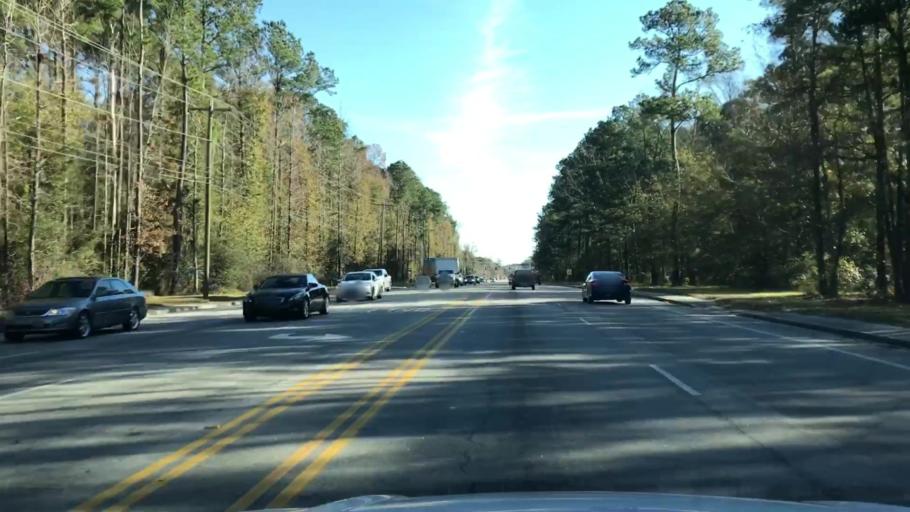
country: US
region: South Carolina
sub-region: Berkeley County
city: Ladson
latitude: 32.9845
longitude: -80.1152
